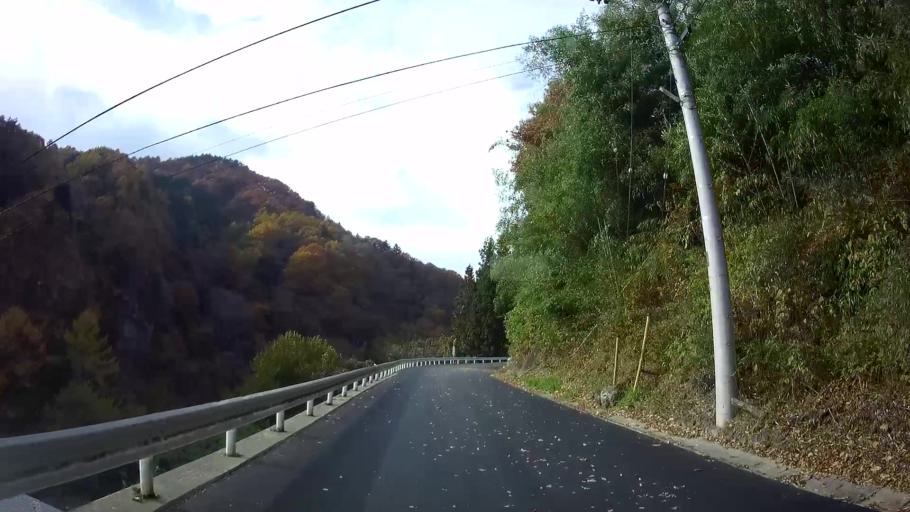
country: JP
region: Gunma
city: Nakanojomachi
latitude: 36.6412
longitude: 138.6504
